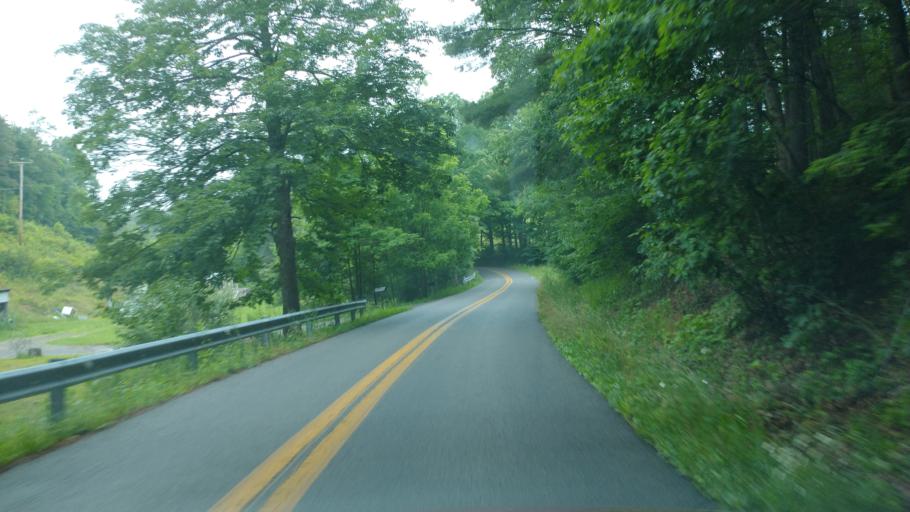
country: US
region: West Virginia
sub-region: Mercer County
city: Athens
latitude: 37.4349
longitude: -80.9689
